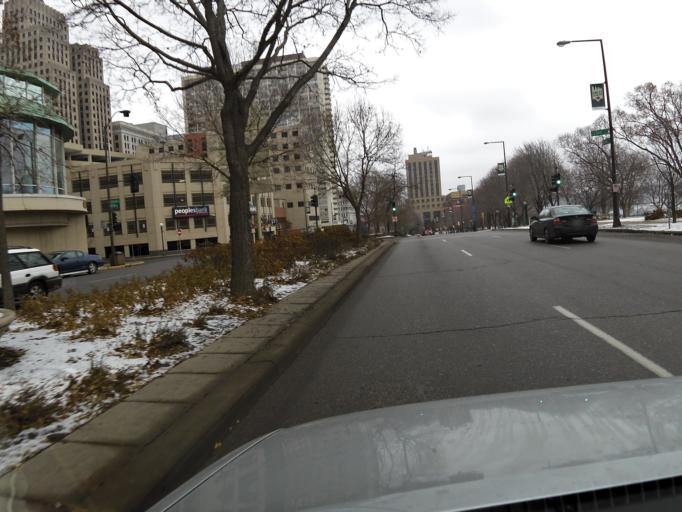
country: US
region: Minnesota
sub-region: Ramsey County
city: Saint Paul
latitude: 44.9442
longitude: -93.0923
